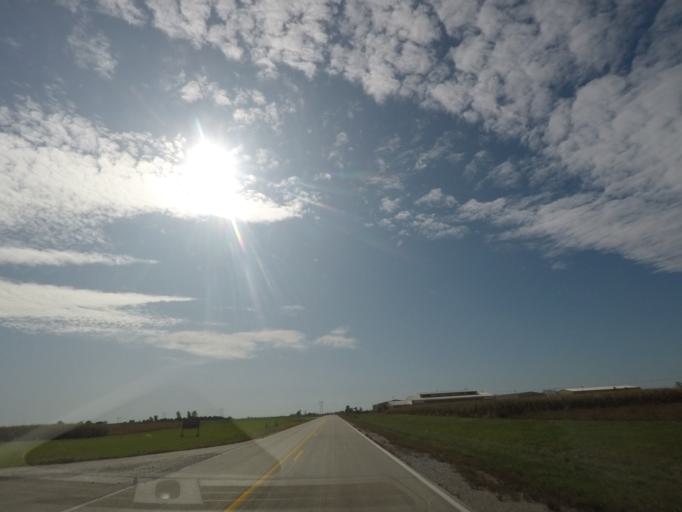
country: US
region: Iowa
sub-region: Boone County
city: Boone
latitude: 42.0219
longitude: -93.7768
